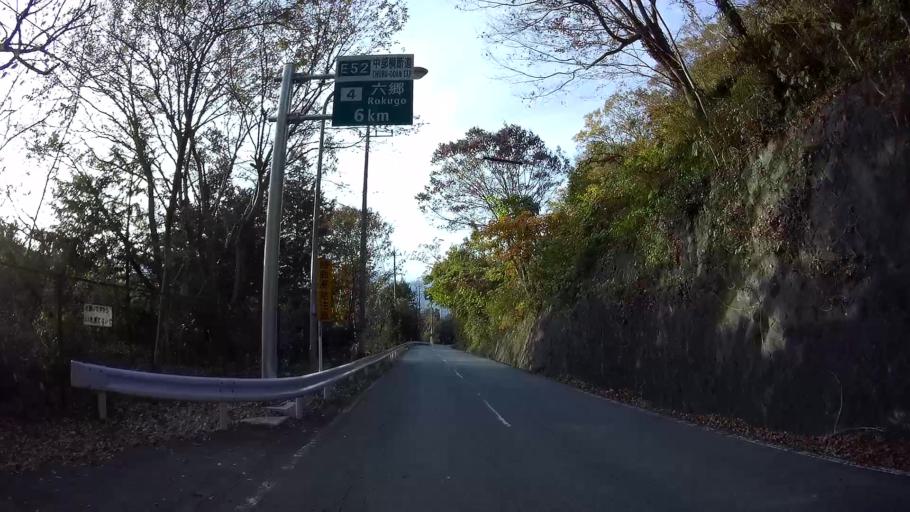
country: JP
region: Yamanashi
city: Ryuo
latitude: 35.4734
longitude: 138.4864
